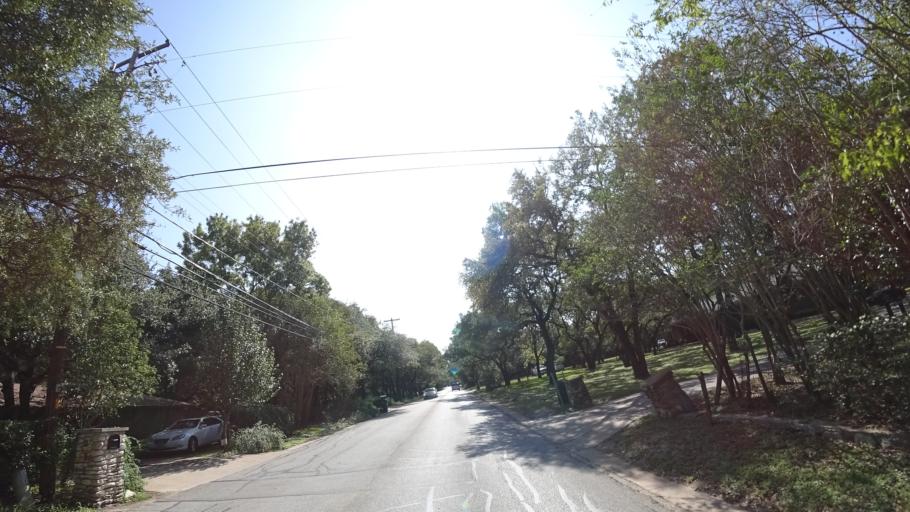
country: US
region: Texas
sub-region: Travis County
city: West Lake Hills
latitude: 30.2841
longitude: -97.8068
